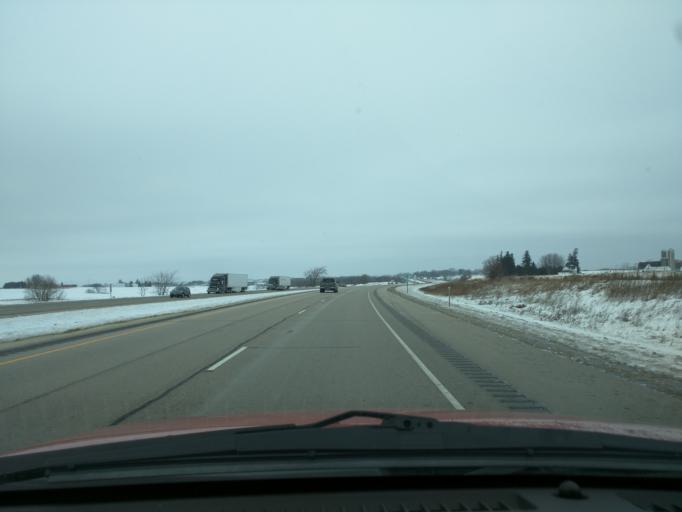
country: US
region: Minnesota
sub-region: Winona County
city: Winona
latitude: 43.9182
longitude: -91.6067
